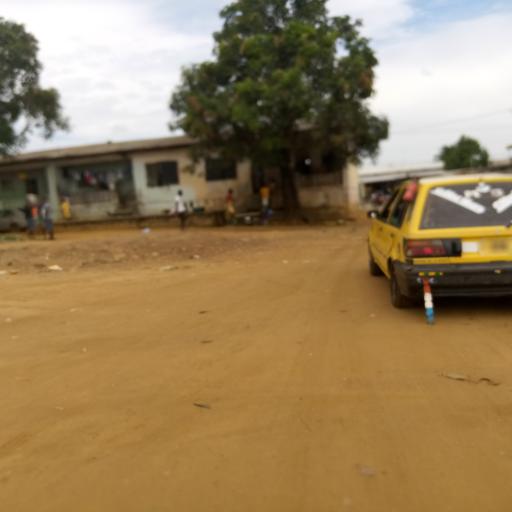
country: LR
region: Montserrado
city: Monrovia
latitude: 6.2969
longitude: -10.7024
